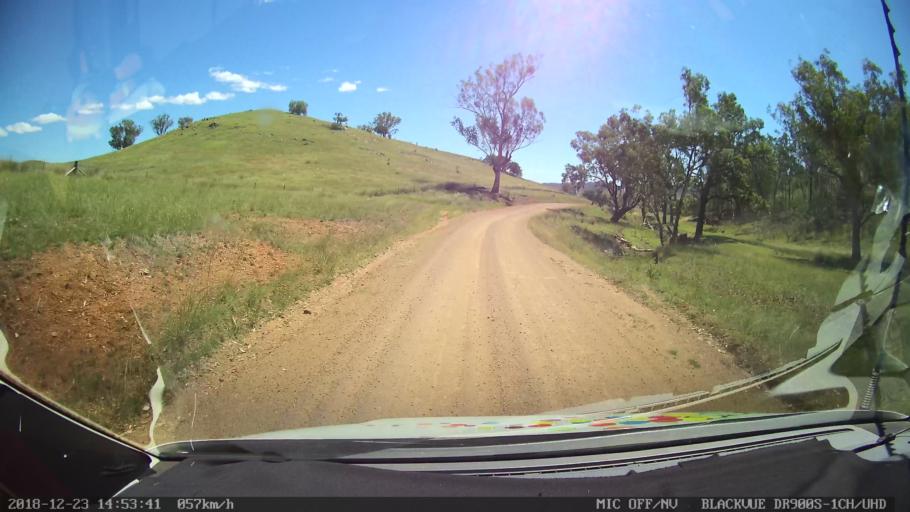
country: AU
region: New South Wales
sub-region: Tamworth Municipality
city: Manilla
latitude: -30.6925
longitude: 150.8510
